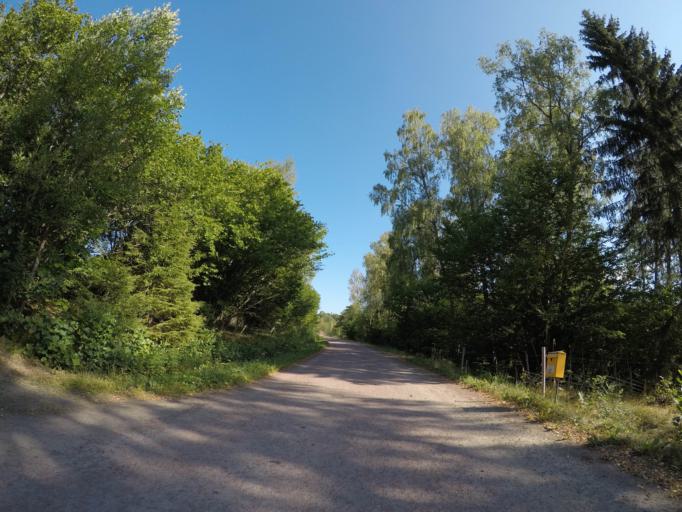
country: AX
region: Alands landsbygd
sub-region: Finstroem
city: Finstroem
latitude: 60.2479
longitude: 19.9217
